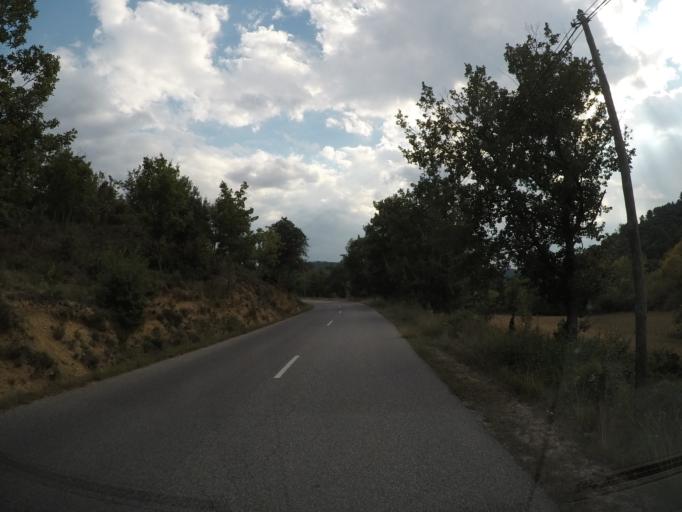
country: FR
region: Provence-Alpes-Cote d'Azur
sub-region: Departement des Alpes-de-Haute-Provence
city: Riez
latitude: 43.8150
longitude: 6.0573
